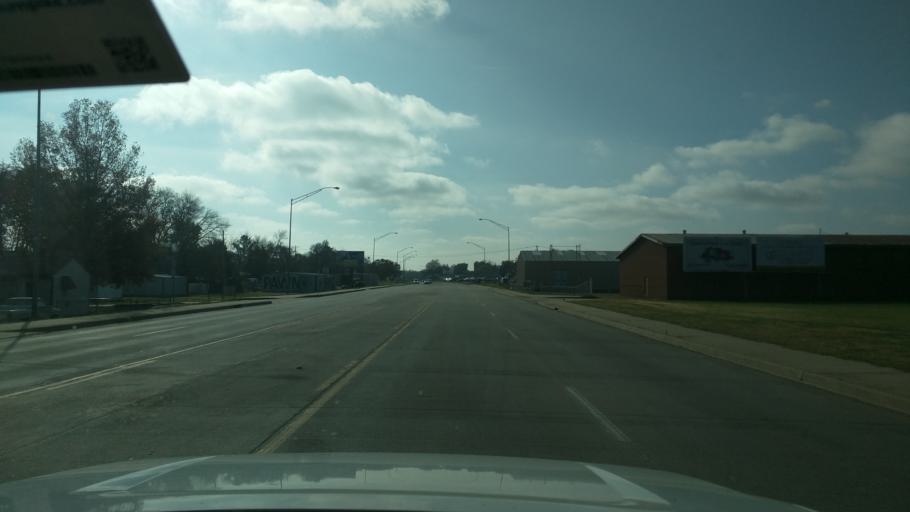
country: US
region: Oklahoma
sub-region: Washington County
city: Dewey
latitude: 36.7956
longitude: -95.9357
